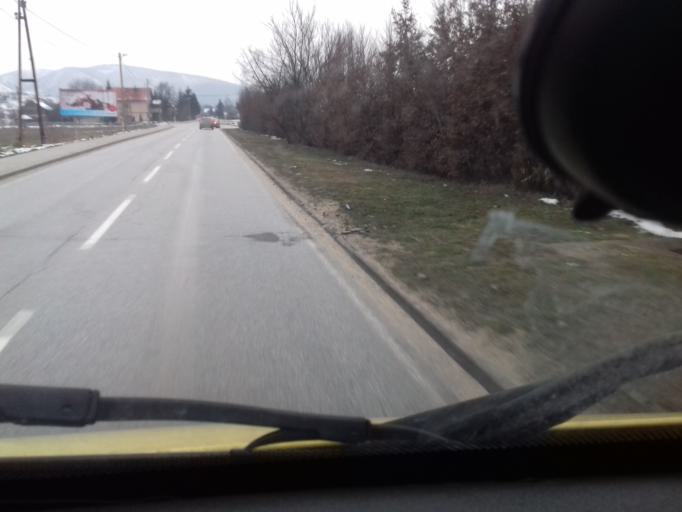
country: BA
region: Federation of Bosnia and Herzegovina
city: Vitez
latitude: 44.1637
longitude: 17.7762
